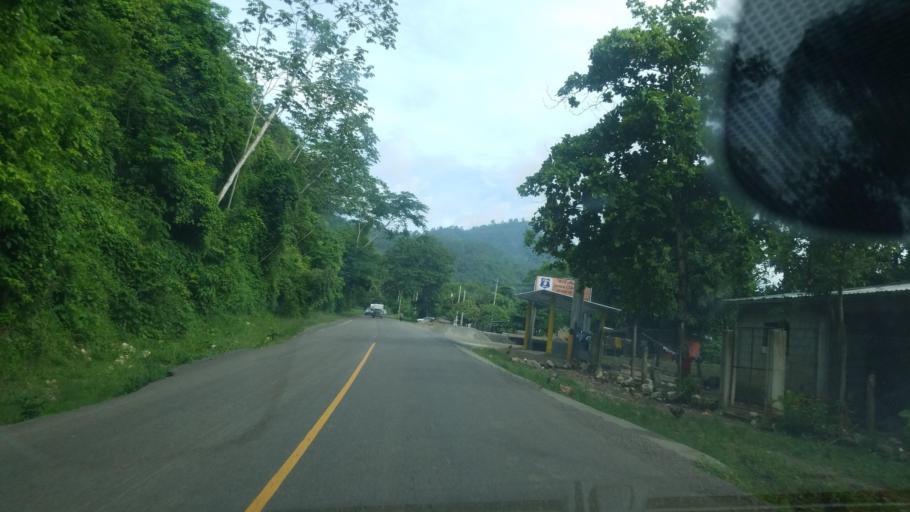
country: HN
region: Santa Barbara
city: Petoa
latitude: 15.2472
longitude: -88.2718
